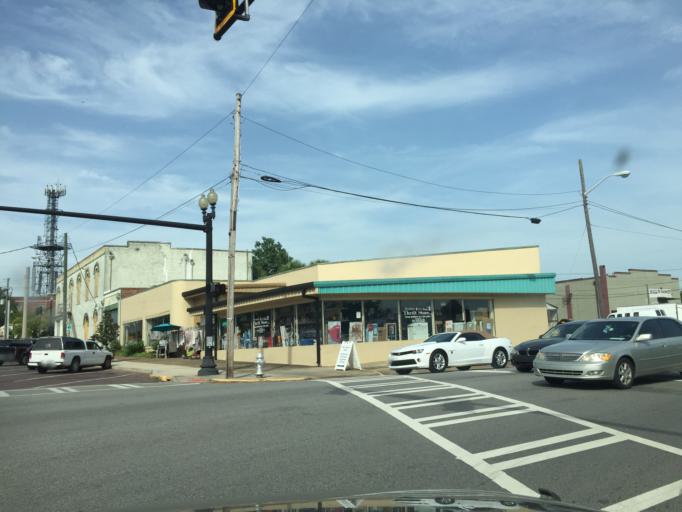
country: US
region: Georgia
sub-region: Thomas County
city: Thomasville
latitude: 30.8358
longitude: -83.9800
